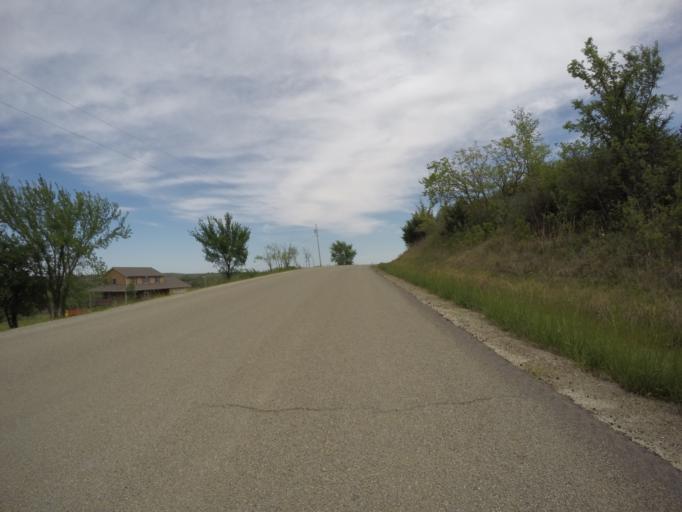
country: US
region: Kansas
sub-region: Riley County
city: Ogden
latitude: 39.0583
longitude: -96.6500
